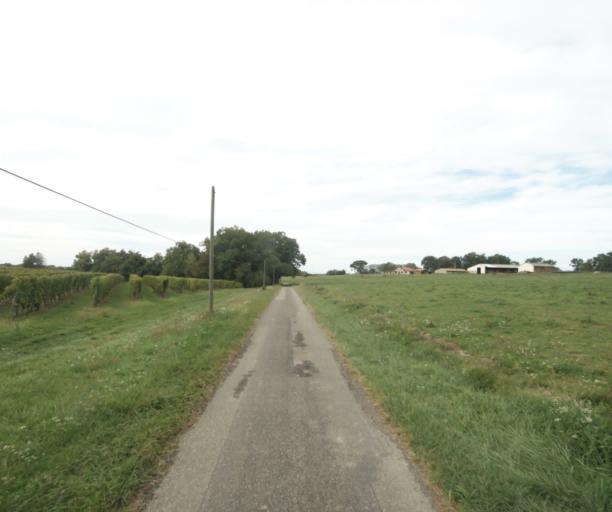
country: FR
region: Midi-Pyrenees
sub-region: Departement du Gers
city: Cazaubon
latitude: 43.8848
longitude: -0.1350
